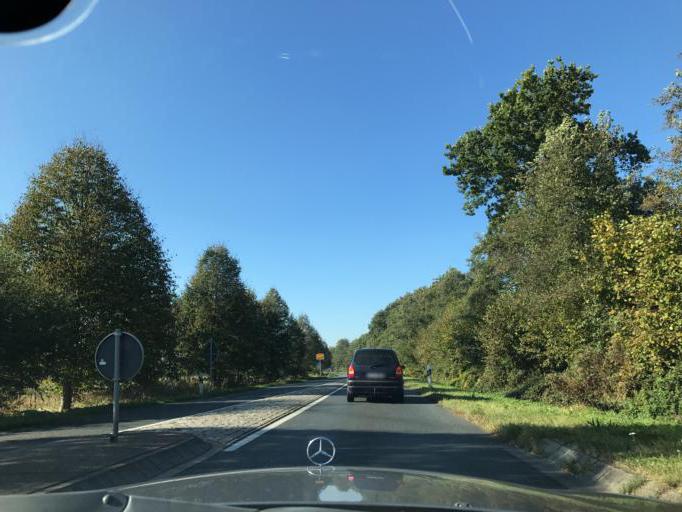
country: DE
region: Lower Saxony
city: Weener
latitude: 53.1289
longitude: 7.3179
